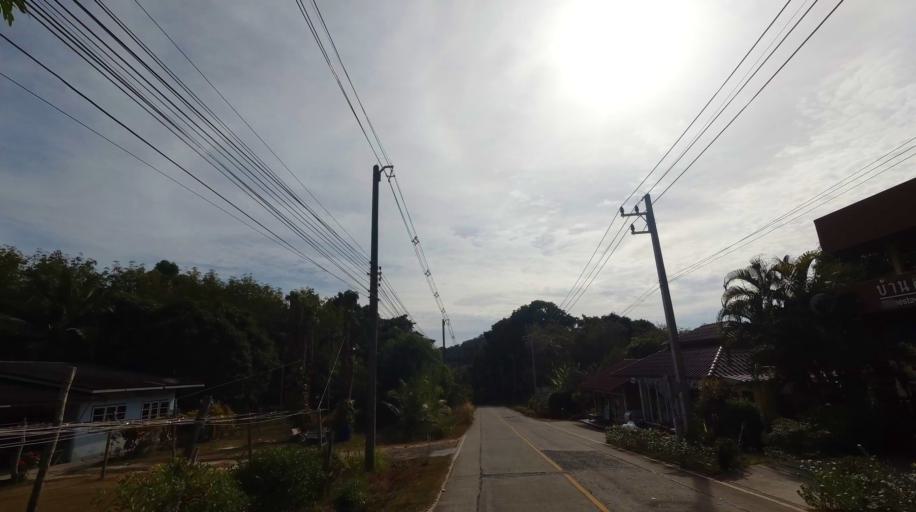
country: TH
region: Trat
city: Ko Kut
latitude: 11.6133
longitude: 102.5428
